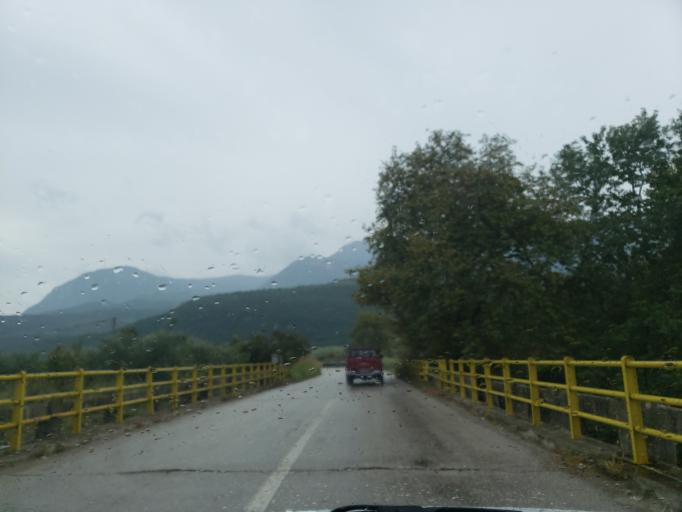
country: GR
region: Central Greece
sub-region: Nomos Fthiotidos
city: Anthili
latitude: 38.8006
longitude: 22.4639
